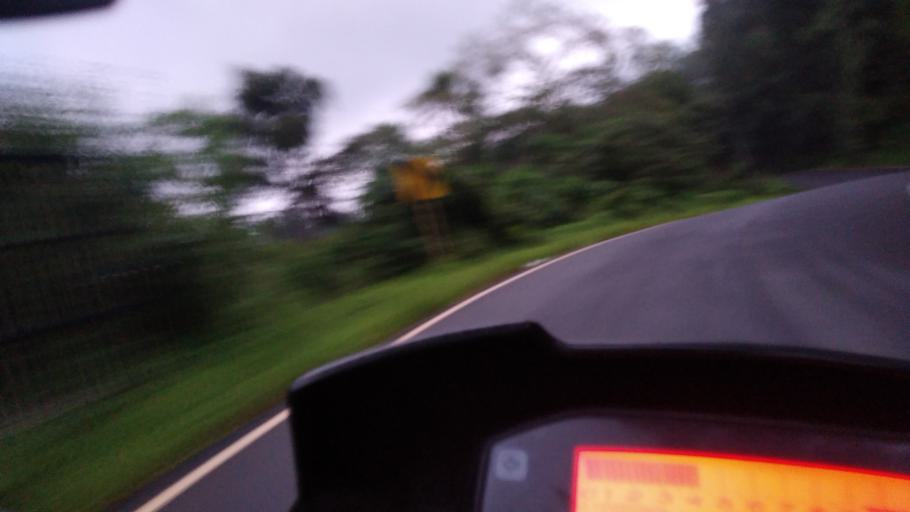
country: IN
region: Kerala
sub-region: Idukki
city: Munnar
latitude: 9.9557
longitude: 77.0835
